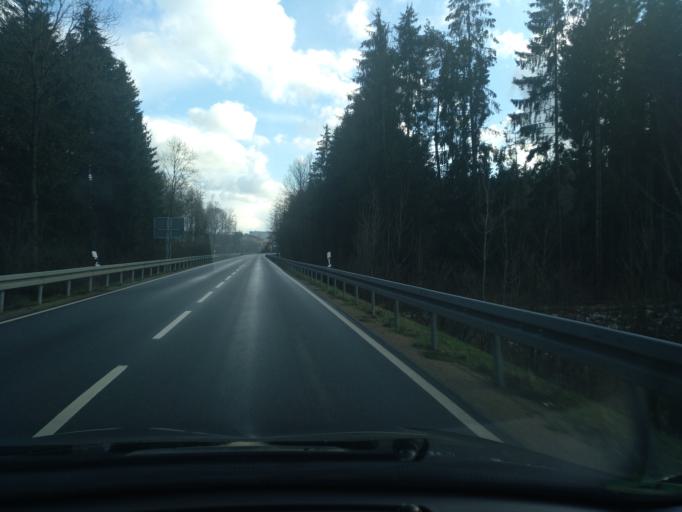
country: DE
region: Bavaria
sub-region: Lower Bavaria
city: Konzell
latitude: 49.0877
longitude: 12.7247
